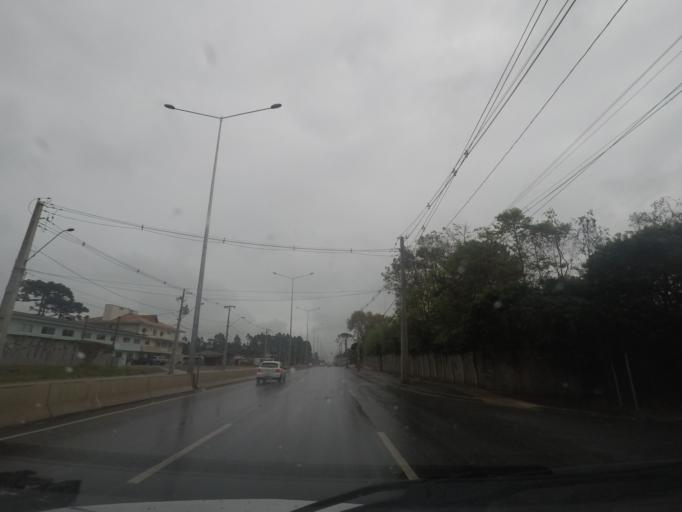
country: BR
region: Parana
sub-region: Piraquara
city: Piraquara
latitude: -25.4604
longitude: -49.0936
